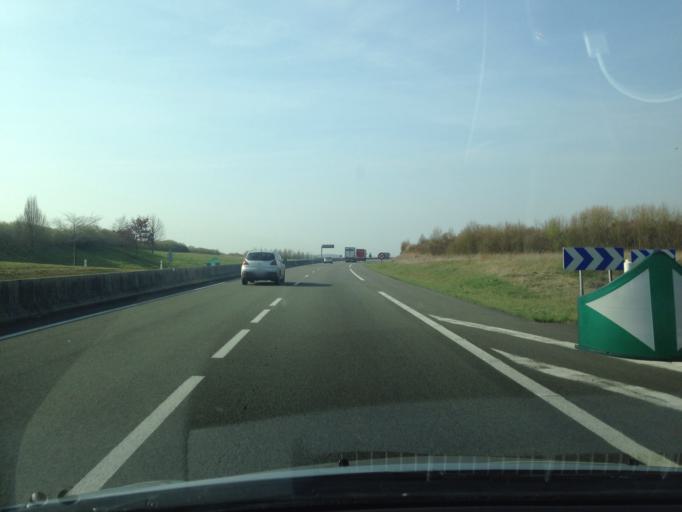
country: FR
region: Picardie
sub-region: Departement de la Somme
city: Sailly-Flibeaucourt
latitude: 50.1681
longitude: 1.7582
